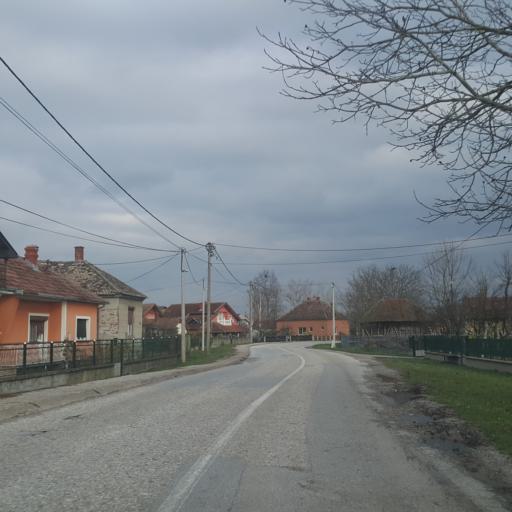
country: RS
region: Central Serbia
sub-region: Sumadijski Okrug
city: Lapovo
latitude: 44.2375
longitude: 21.1019
